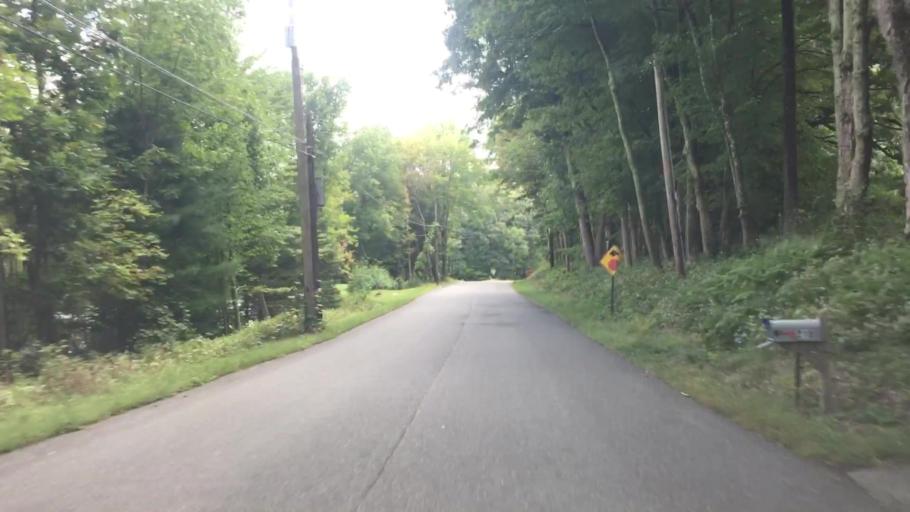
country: US
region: Connecticut
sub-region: Tolland County
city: Stafford Springs
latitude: 41.9195
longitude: -72.2273
